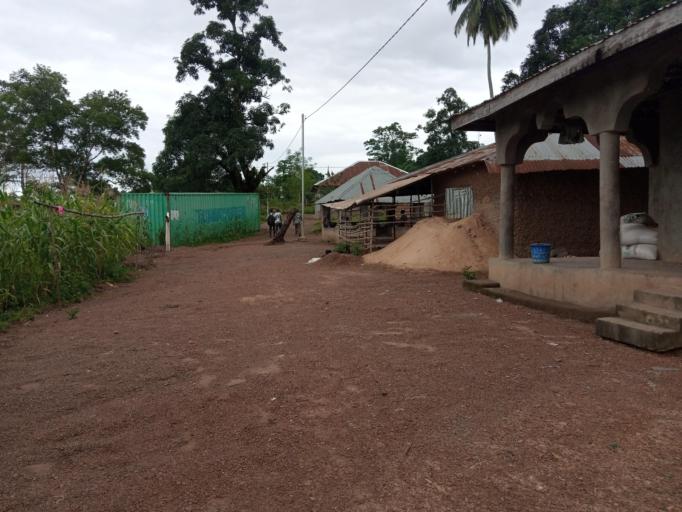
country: SL
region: Southern Province
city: Largo
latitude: 8.2021
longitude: -12.0563
